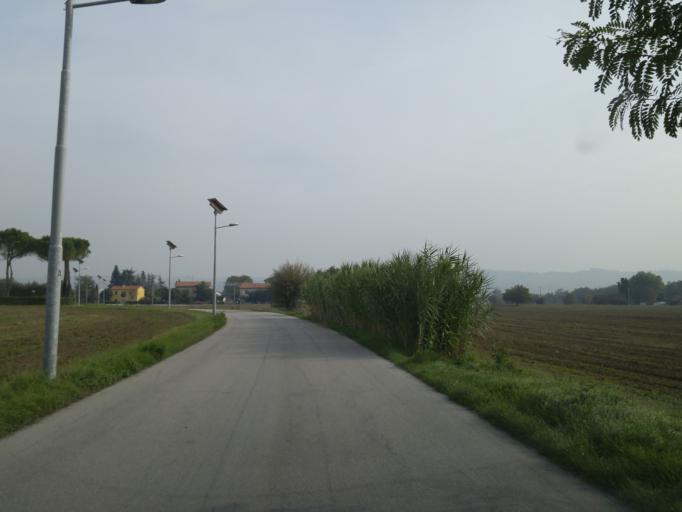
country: IT
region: The Marches
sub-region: Provincia di Pesaro e Urbino
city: Lucrezia
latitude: 43.7691
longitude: 12.9394
